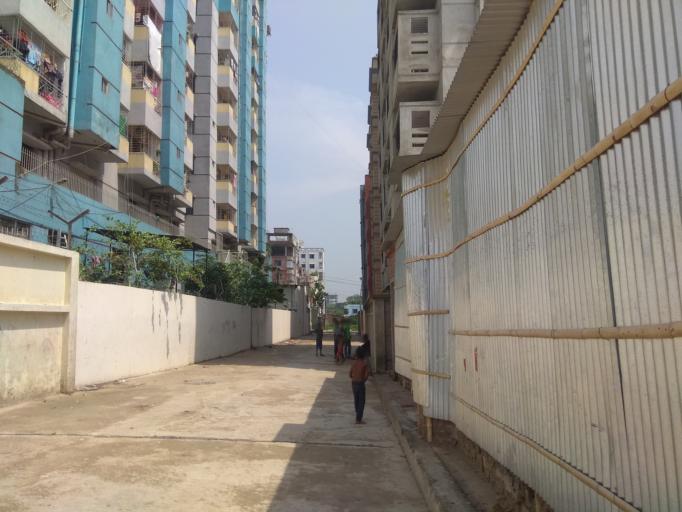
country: BD
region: Dhaka
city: Azimpur
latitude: 23.8074
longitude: 90.3544
